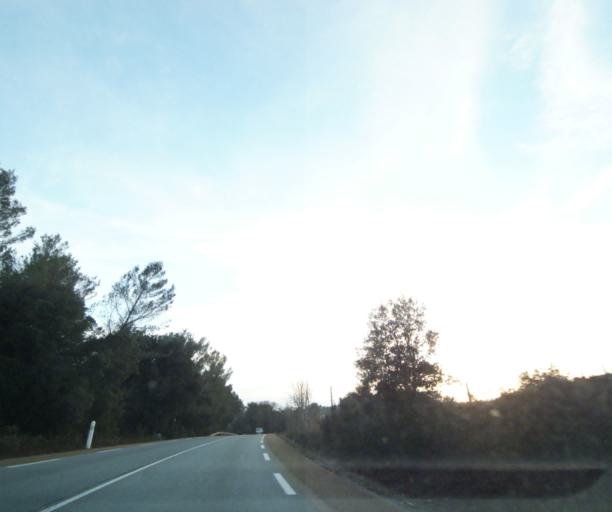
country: FR
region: Provence-Alpes-Cote d'Azur
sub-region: Departement du Var
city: La Motte
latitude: 43.4867
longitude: 6.5119
